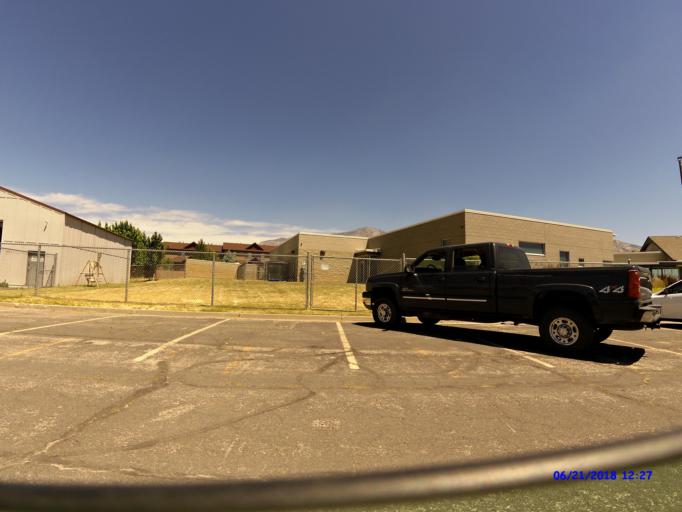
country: US
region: Utah
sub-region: Weber County
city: Harrisville
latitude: 41.2823
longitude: -111.9981
